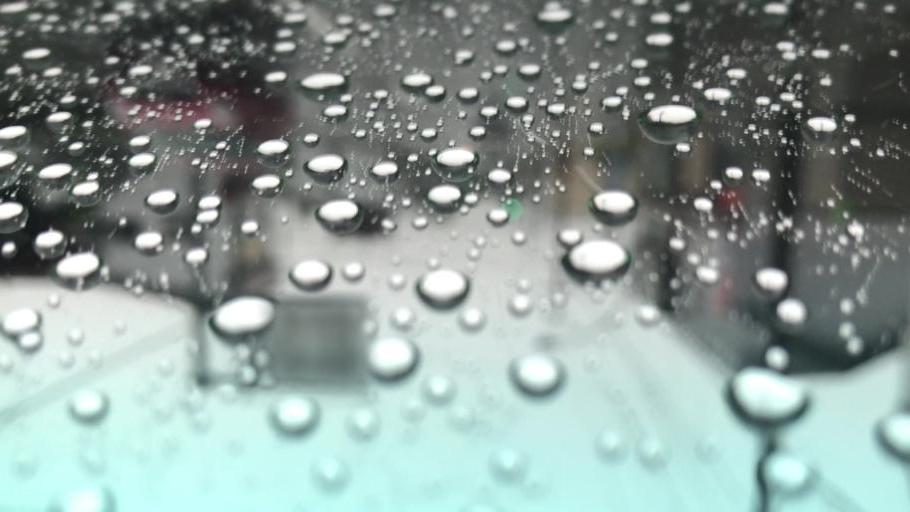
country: JP
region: Hokkaido
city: Nayoro
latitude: 44.2921
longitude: 142.4193
